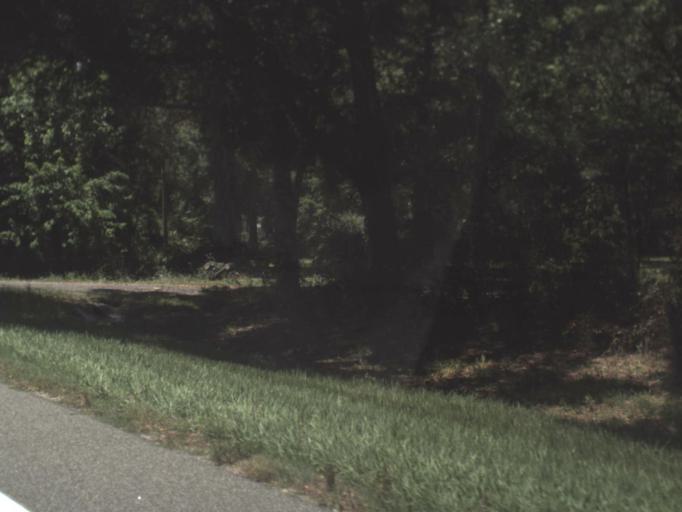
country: US
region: Florida
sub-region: Lafayette County
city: Mayo
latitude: 29.9657
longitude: -82.9750
